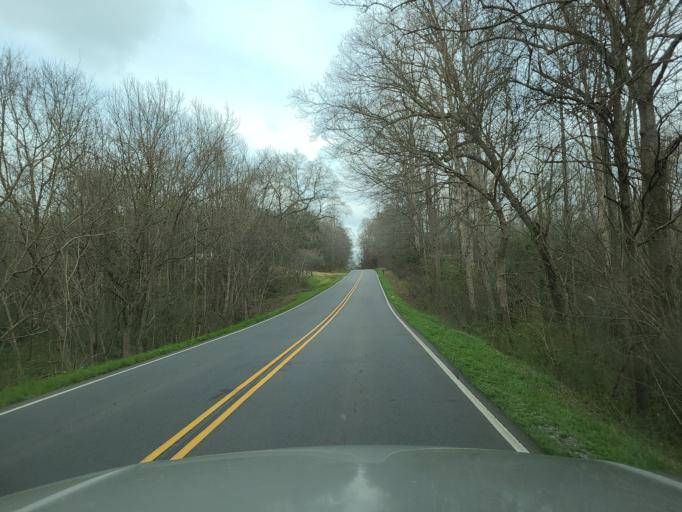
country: US
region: North Carolina
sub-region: Cleveland County
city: Boiling Springs
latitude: 35.2556
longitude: -81.6934
